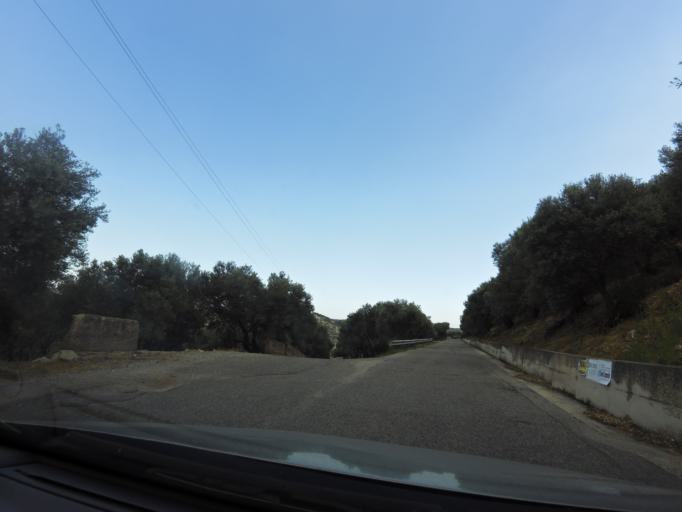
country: IT
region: Calabria
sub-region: Provincia di Reggio Calabria
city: Camini
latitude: 38.4608
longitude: 16.5020
